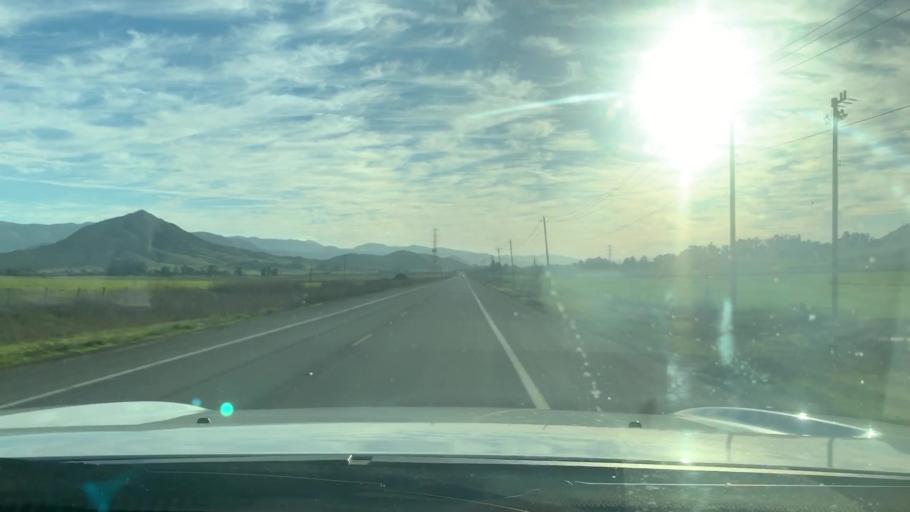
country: US
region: California
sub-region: San Luis Obispo County
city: San Luis Obispo
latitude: 35.2844
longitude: -120.7330
